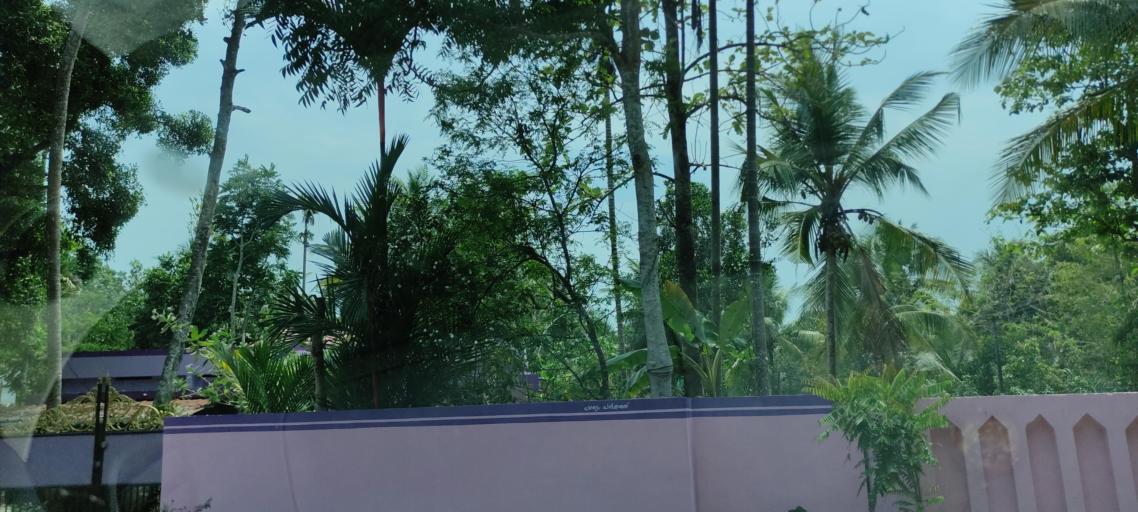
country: IN
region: Kerala
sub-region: Alappuzha
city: Vayalar
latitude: 9.7117
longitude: 76.3398
